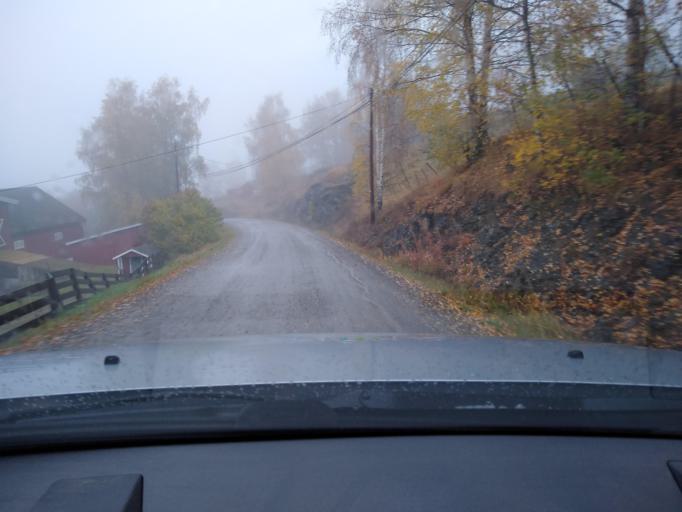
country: NO
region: Oppland
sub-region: Ringebu
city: Ringebu
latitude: 61.5288
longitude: 10.1569
